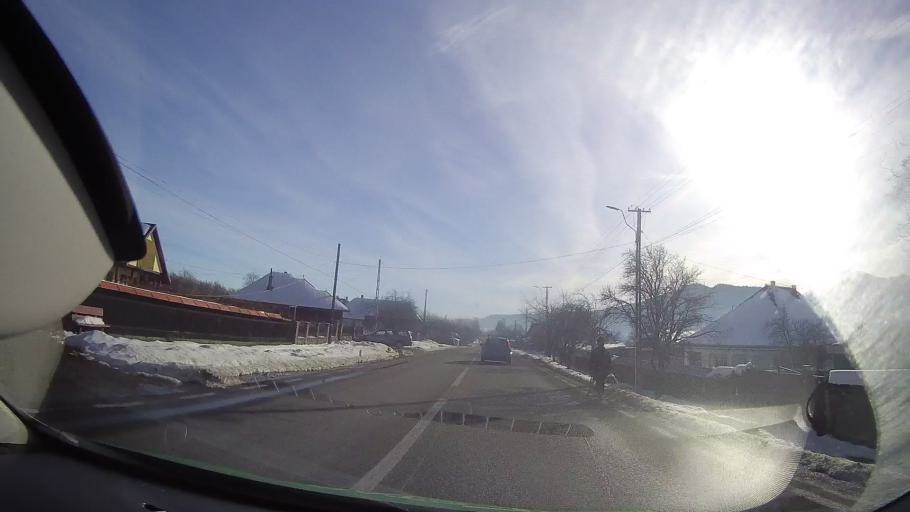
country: RO
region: Neamt
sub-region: Comuna Cracaoani
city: Cracaoani
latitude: 47.1019
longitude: 26.3079
